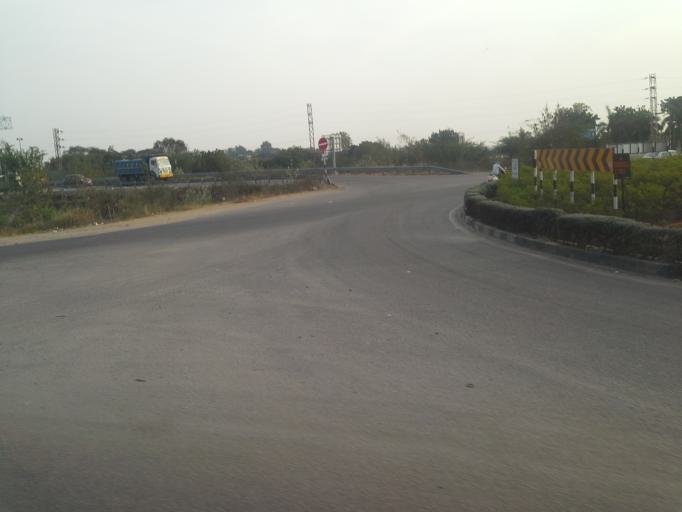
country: IN
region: Telangana
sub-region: Hyderabad
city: Hyderabad
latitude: 17.3491
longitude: 78.3587
